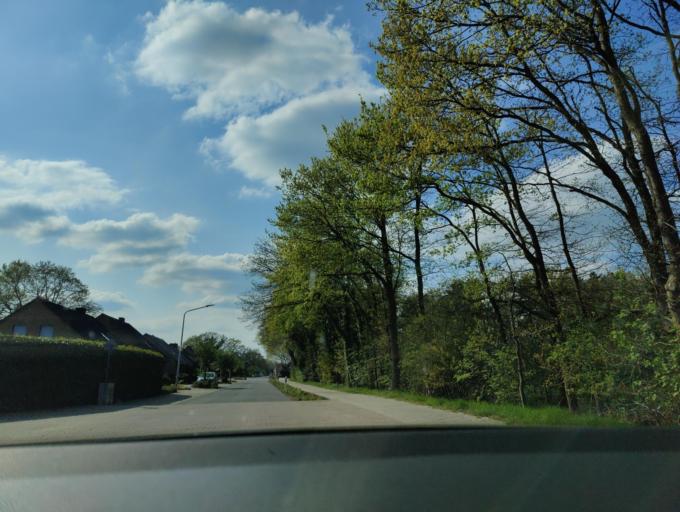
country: DE
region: Lower Saxony
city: Emsburen
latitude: 52.3853
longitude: 7.3091
